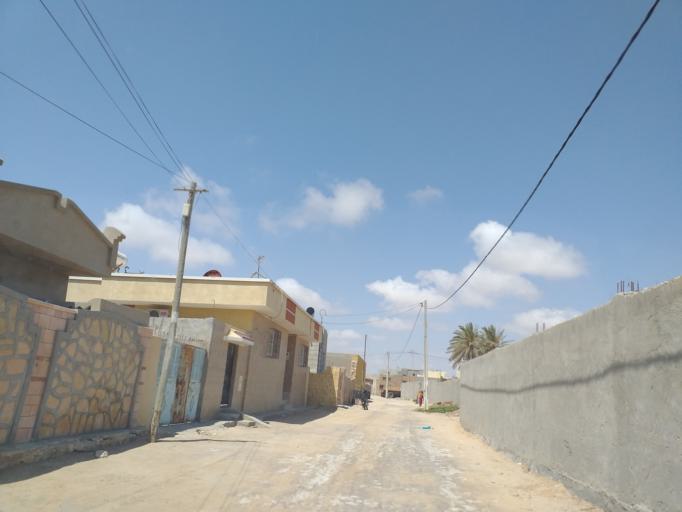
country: TN
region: Qabis
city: Gabes
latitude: 33.9480
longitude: 10.0586
